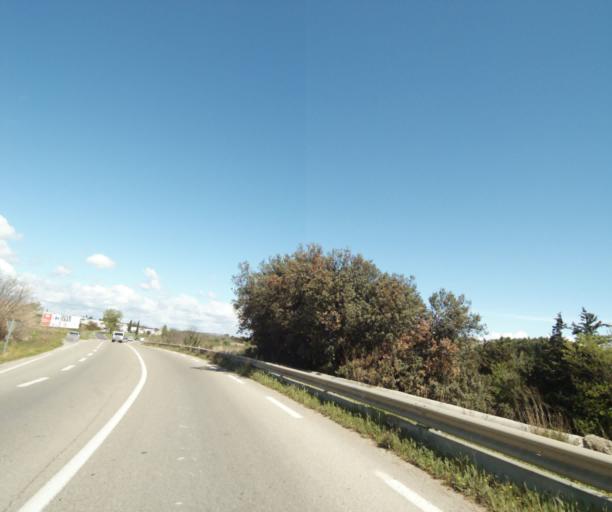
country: FR
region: Languedoc-Roussillon
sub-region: Departement de l'Herault
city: Villeneuve-les-Maguelone
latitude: 43.5565
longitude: 3.8487
